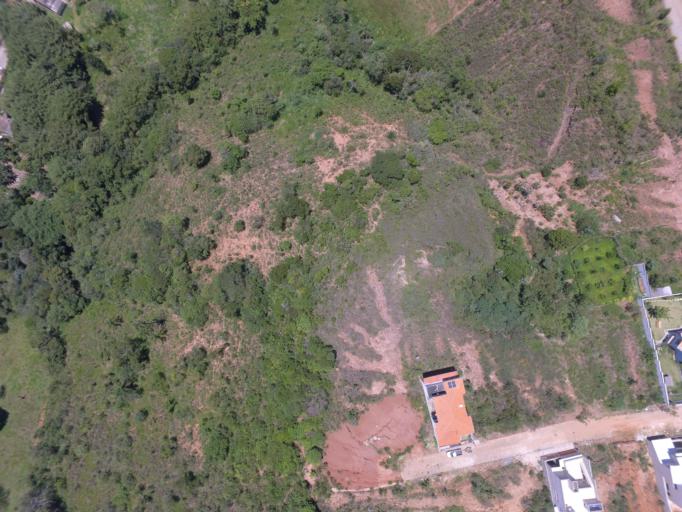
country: BR
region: Minas Gerais
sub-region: Tiradentes
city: Tiradentes
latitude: -21.0649
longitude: -44.0803
